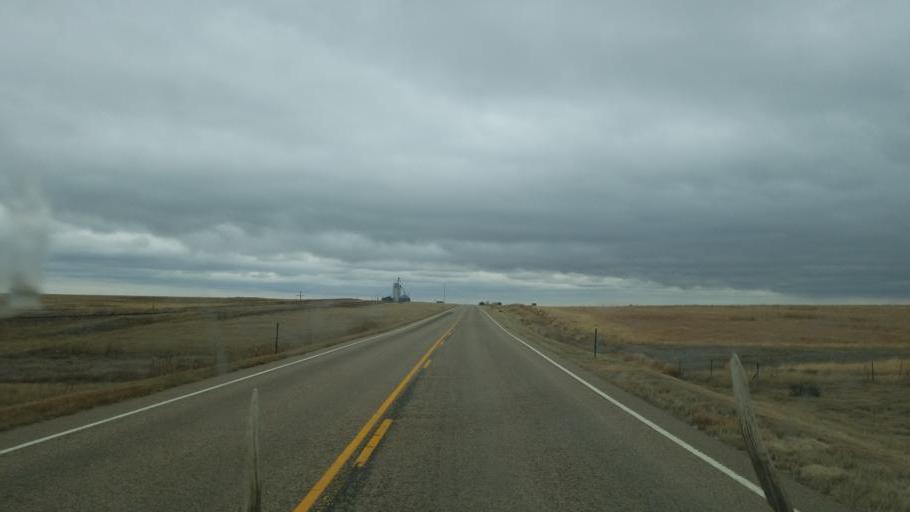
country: US
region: Colorado
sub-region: Cheyenne County
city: Cheyenne Wells
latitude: 38.8159
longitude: -102.5519
